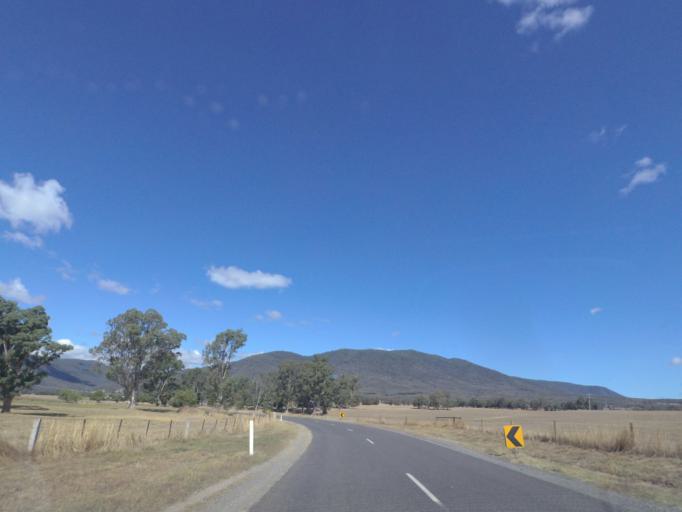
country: AU
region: Victoria
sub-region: Murrindindi
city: Alexandra
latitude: -37.2856
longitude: 145.8037
